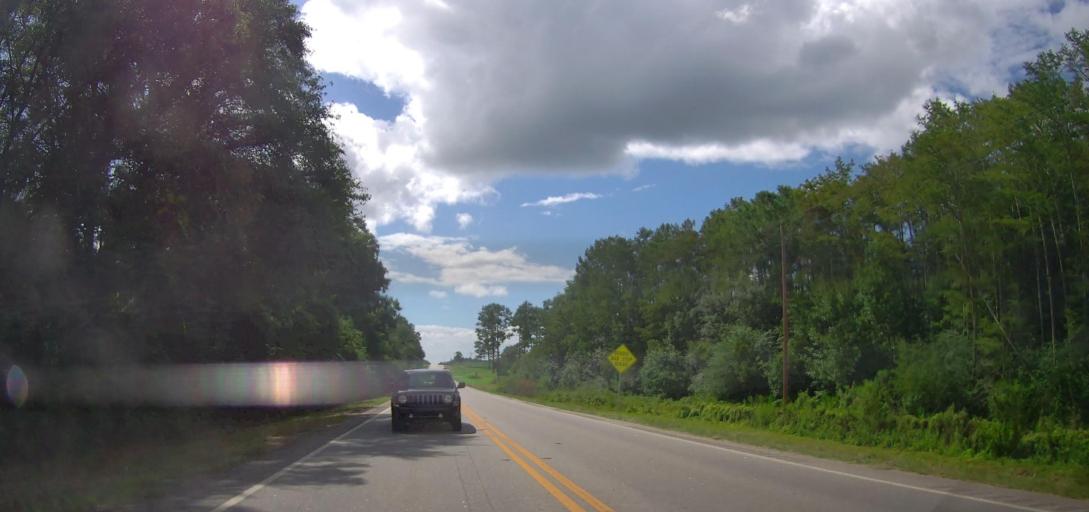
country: US
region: Georgia
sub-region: Coffee County
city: Broxton
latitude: 31.5603
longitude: -82.9820
